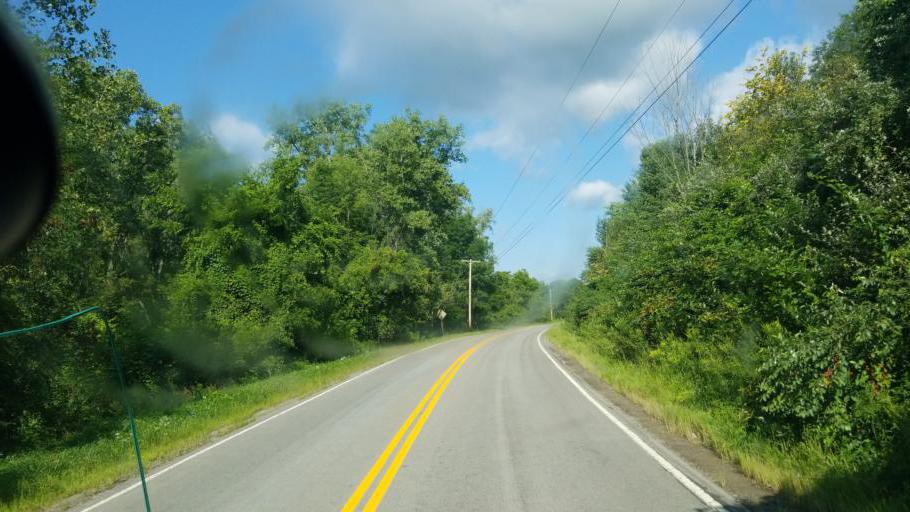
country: US
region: New York
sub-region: Steuben County
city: Canisteo
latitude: 42.2866
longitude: -77.6093
